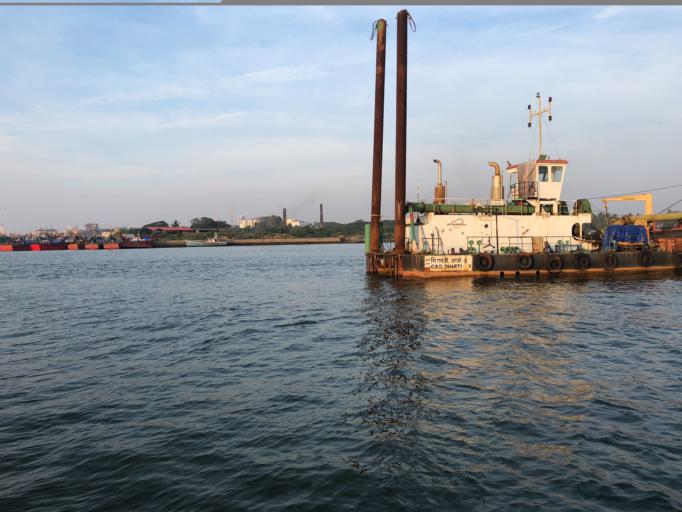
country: IN
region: Karnataka
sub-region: Dakshina Kannada
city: Ullal
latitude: 12.8473
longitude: 74.8318
